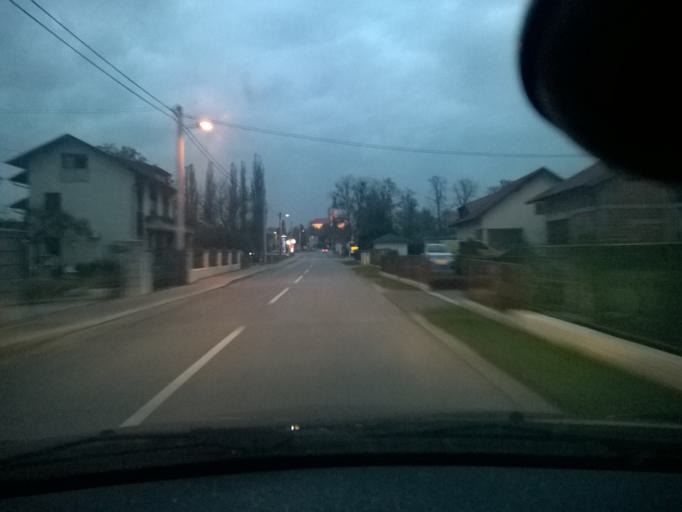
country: HR
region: Krapinsko-Zagorska
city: Zabok
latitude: 46.0764
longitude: 15.9069
